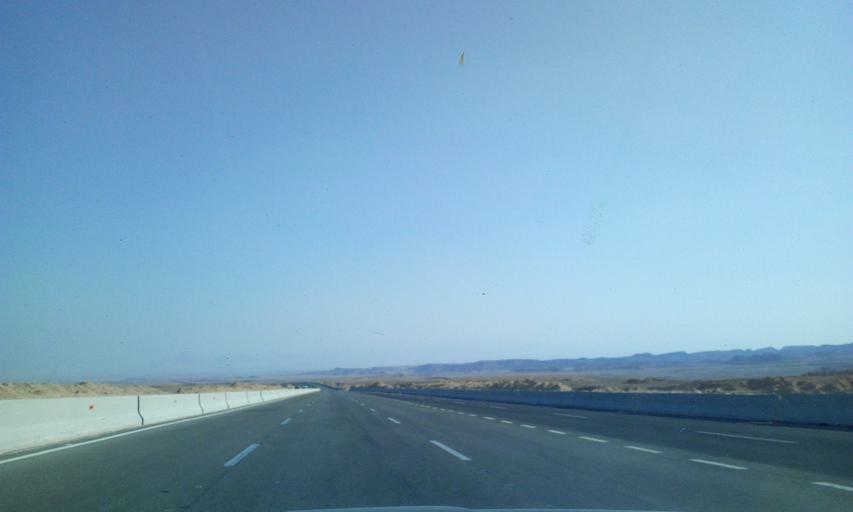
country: EG
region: As Suways
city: Ain Sukhna
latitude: 29.2805
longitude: 32.4686
